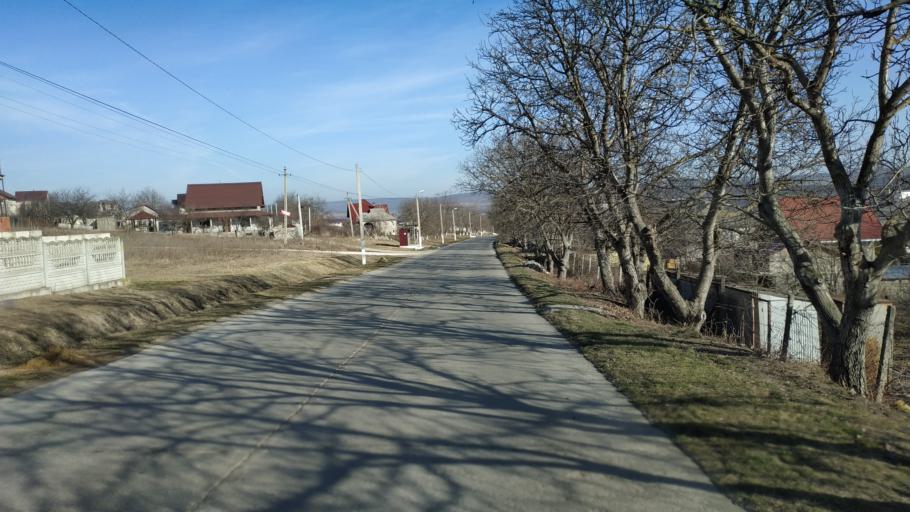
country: MD
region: Chisinau
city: Vatra
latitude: 46.9929
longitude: 28.6737
